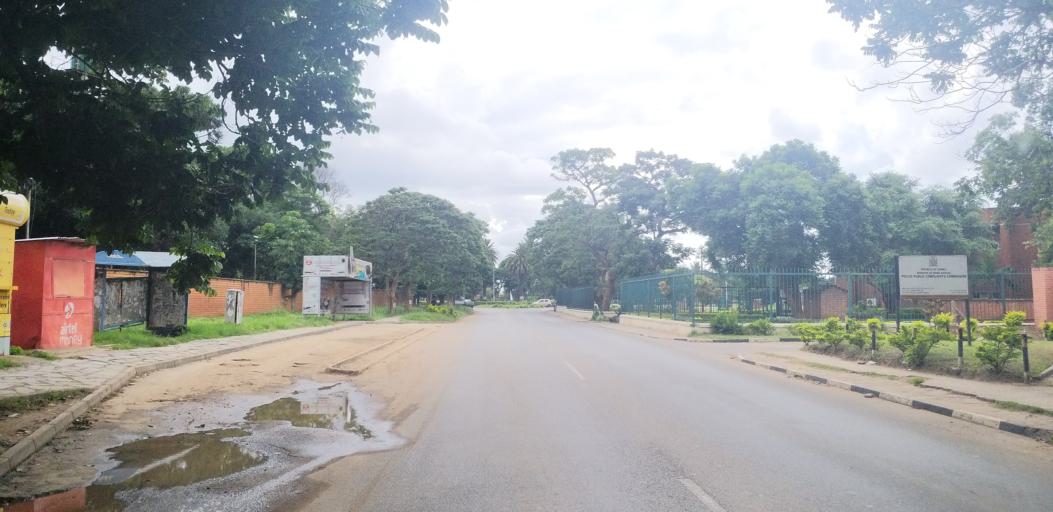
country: ZM
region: Lusaka
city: Lusaka
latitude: -15.4195
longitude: 28.3073
